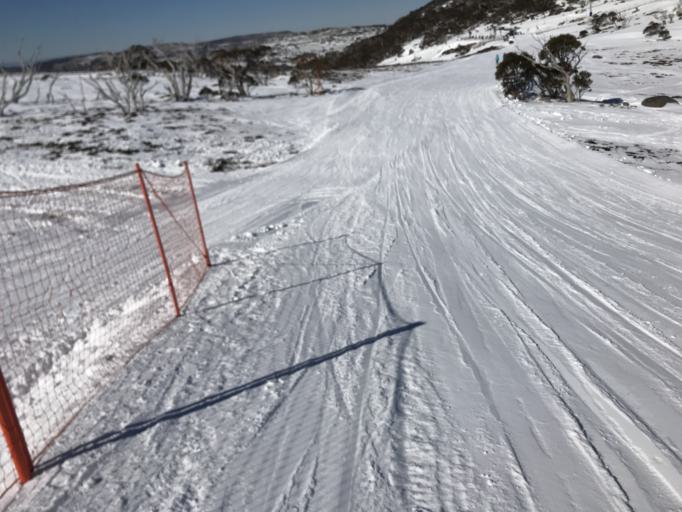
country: AU
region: New South Wales
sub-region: Snowy River
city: Jindabyne
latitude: -36.3820
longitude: 148.3917
